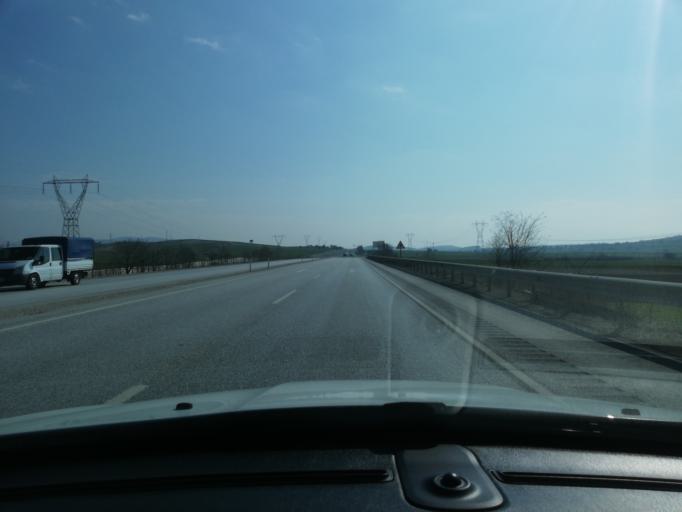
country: TR
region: Cankiri
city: Kursunlu
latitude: 40.8424
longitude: 33.1752
